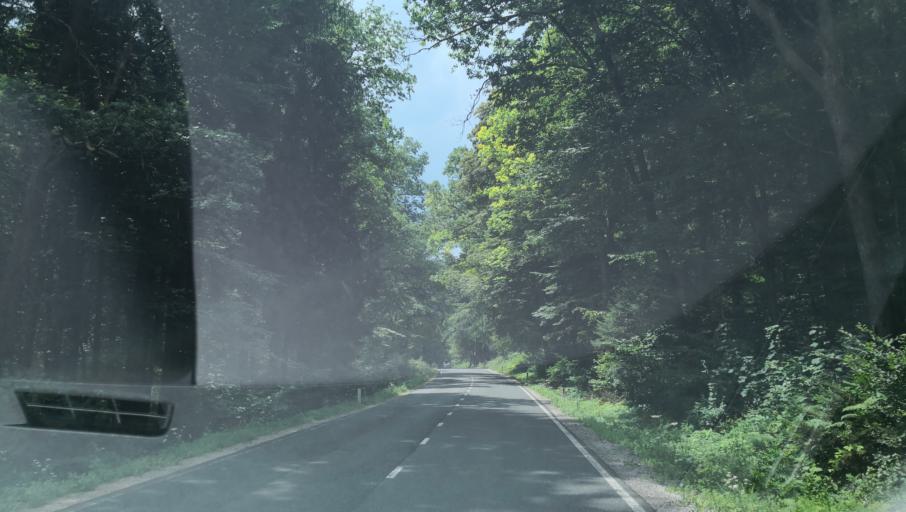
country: SI
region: Ivancna Gorica
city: Ivancna Gorica
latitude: 45.8919
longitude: 14.7983
